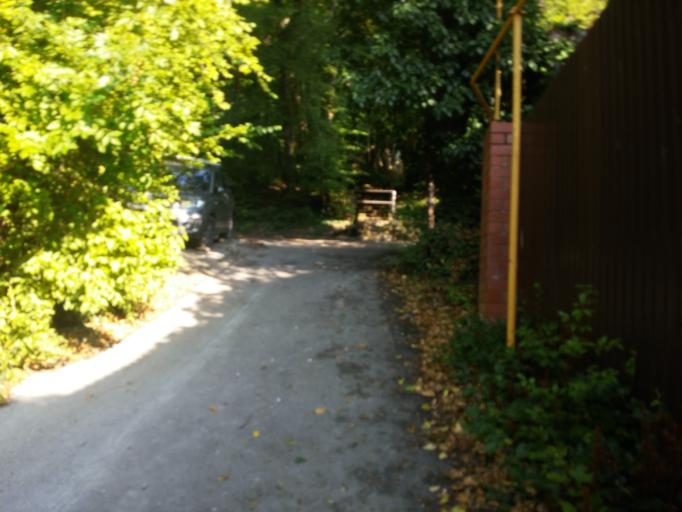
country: RU
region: Krasnodarskiy
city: Divnomorskoye
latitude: 44.4657
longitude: 38.1615
